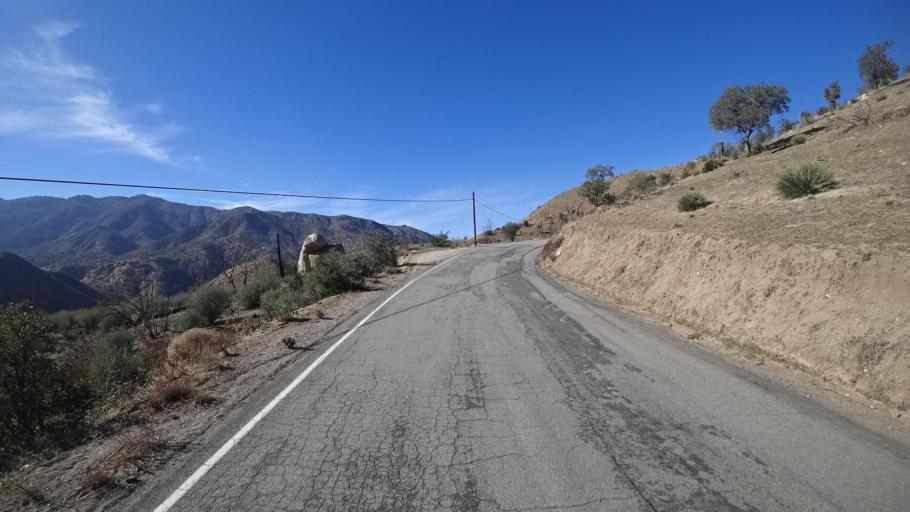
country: US
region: California
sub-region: Kern County
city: Bodfish
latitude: 35.5569
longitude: -118.5089
